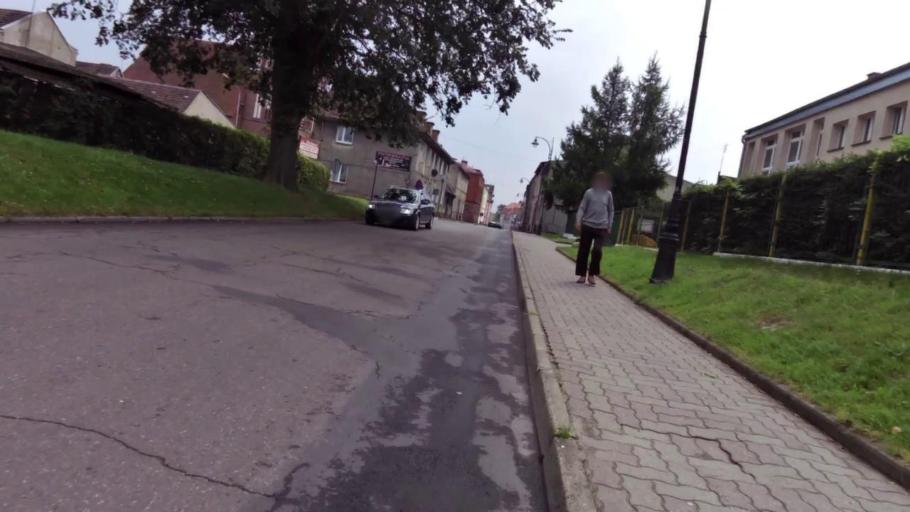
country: PL
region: West Pomeranian Voivodeship
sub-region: Powiat drawski
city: Drawsko Pomorskie
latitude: 53.5321
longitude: 15.8095
